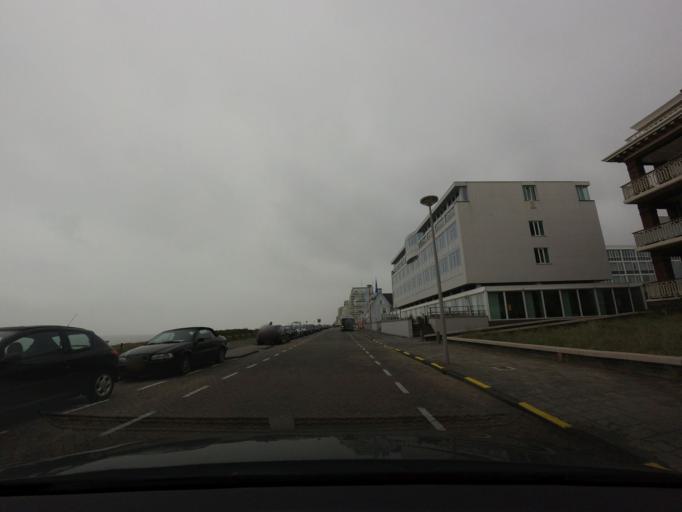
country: NL
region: South Holland
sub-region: Gemeente Noordwijk
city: Noordwijk-Binnen
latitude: 52.2388
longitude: 4.4253
